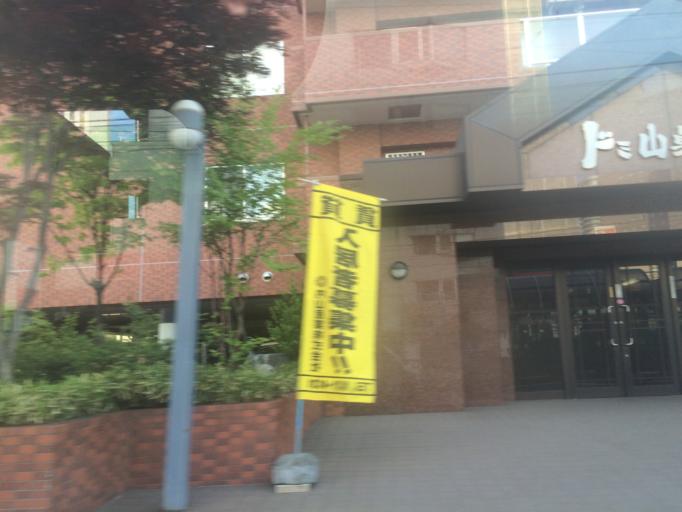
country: JP
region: Hokkaido
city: Sapporo
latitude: 43.0483
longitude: 141.3498
